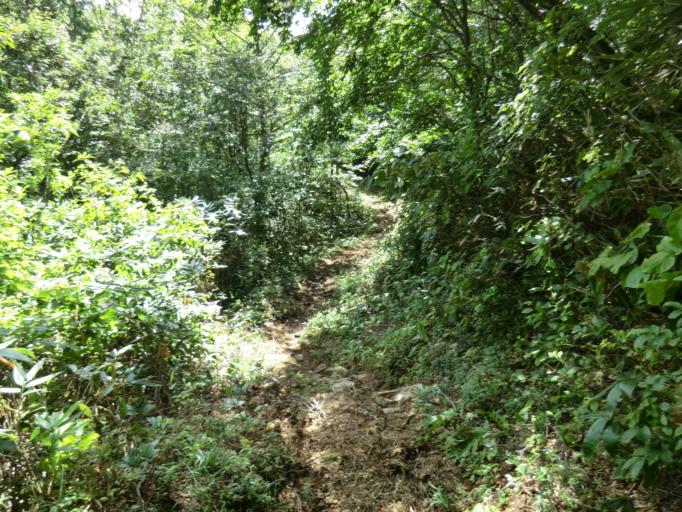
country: JP
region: Fukushima
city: Fukushima-shi
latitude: 37.7519
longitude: 140.2834
